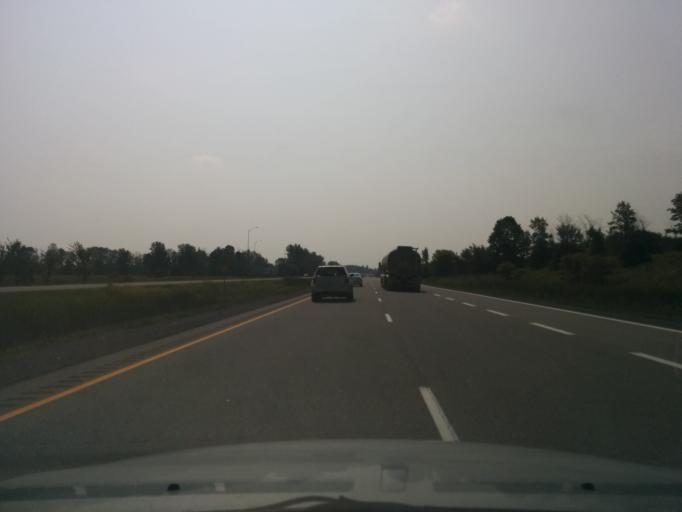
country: CA
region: Ontario
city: Bells Corners
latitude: 45.1452
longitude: -75.6803
